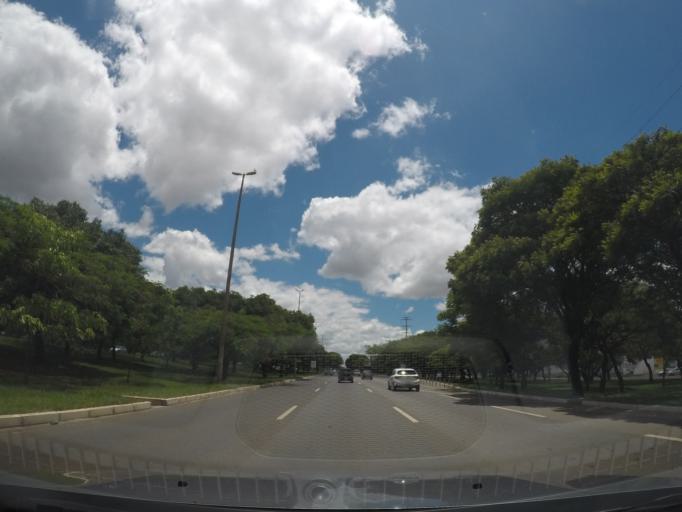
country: BR
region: Federal District
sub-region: Brasilia
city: Brasilia
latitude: -15.7967
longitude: -47.9453
